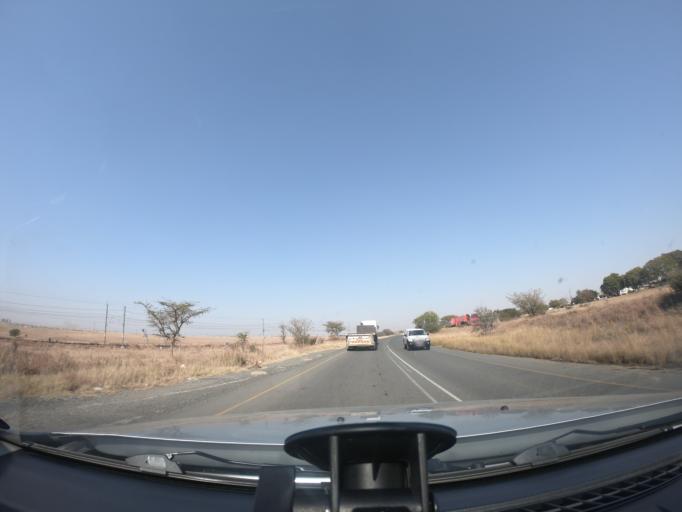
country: ZA
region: KwaZulu-Natal
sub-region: uThukela District Municipality
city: Ladysmith
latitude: -28.7532
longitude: 29.8228
